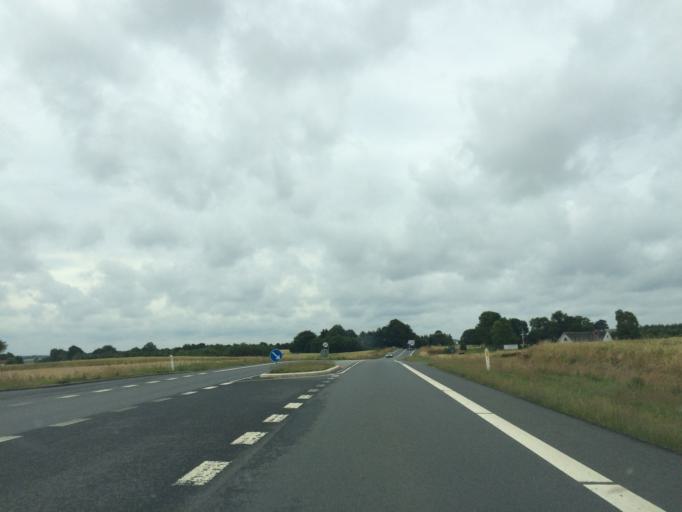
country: DK
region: Central Jutland
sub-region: Silkeborg Kommune
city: Svejbaek
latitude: 56.2198
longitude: 9.6245
